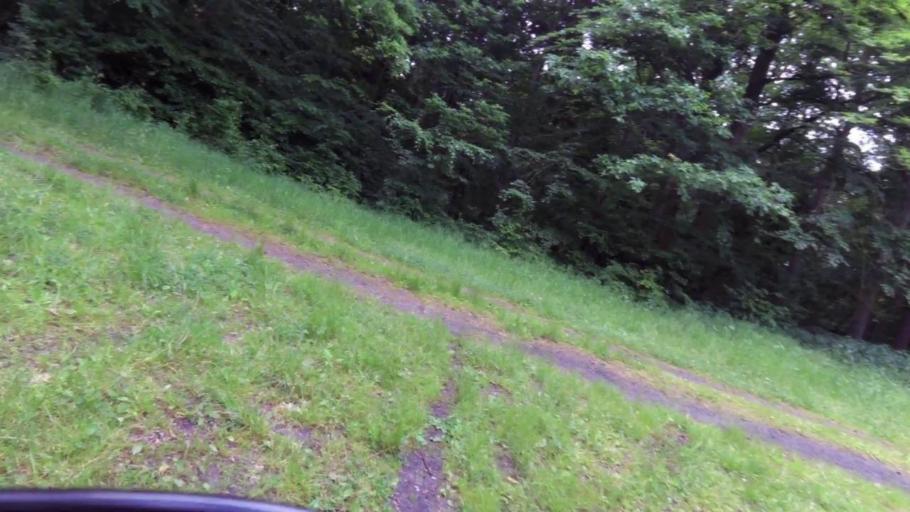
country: PL
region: West Pomeranian Voivodeship
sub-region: Powiat kamienski
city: Miedzyzdroje
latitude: 53.8818
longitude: 14.4885
